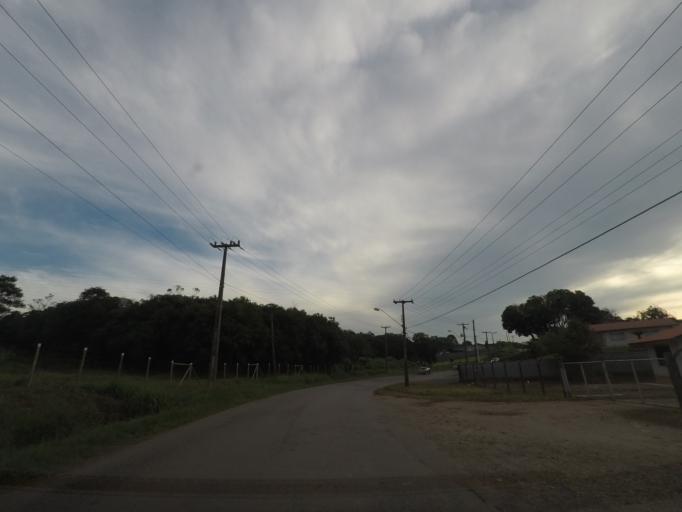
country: BR
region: Parana
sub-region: Colombo
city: Colombo
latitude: -25.2878
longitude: -49.2024
